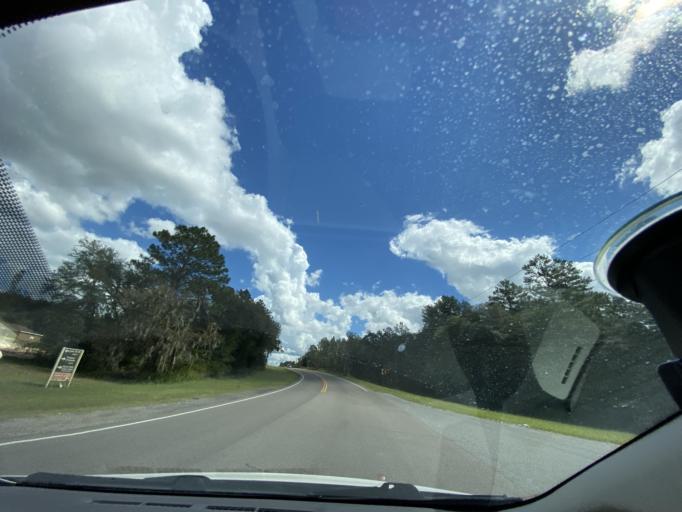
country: US
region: Florida
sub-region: Citrus County
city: Hernando
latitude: 29.0265
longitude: -82.2502
